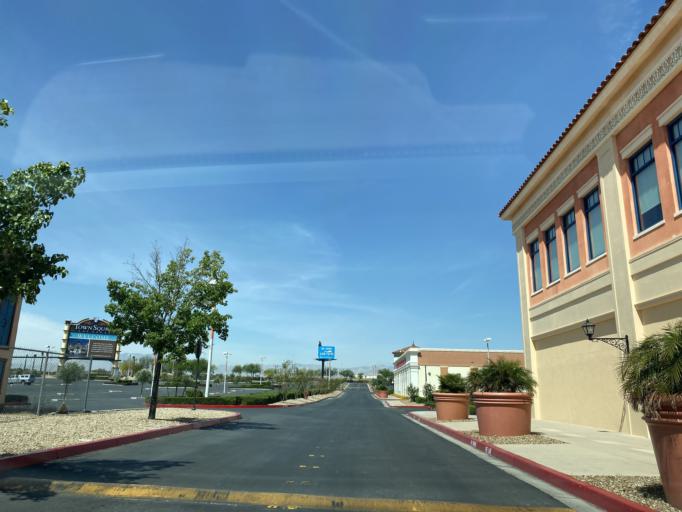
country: US
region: Nevada
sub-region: Clark County
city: Paradise
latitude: 36.0664
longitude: -115.1771
